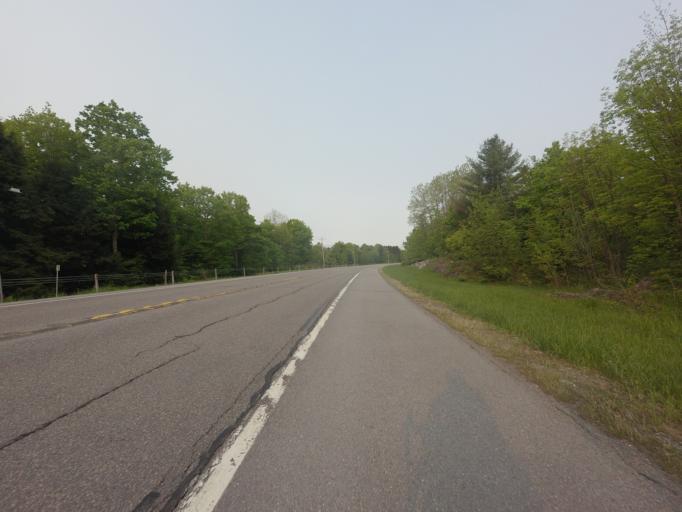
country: US
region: New York
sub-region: Jefferson County
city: Carthage
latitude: 44.0742
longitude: -75.4565
